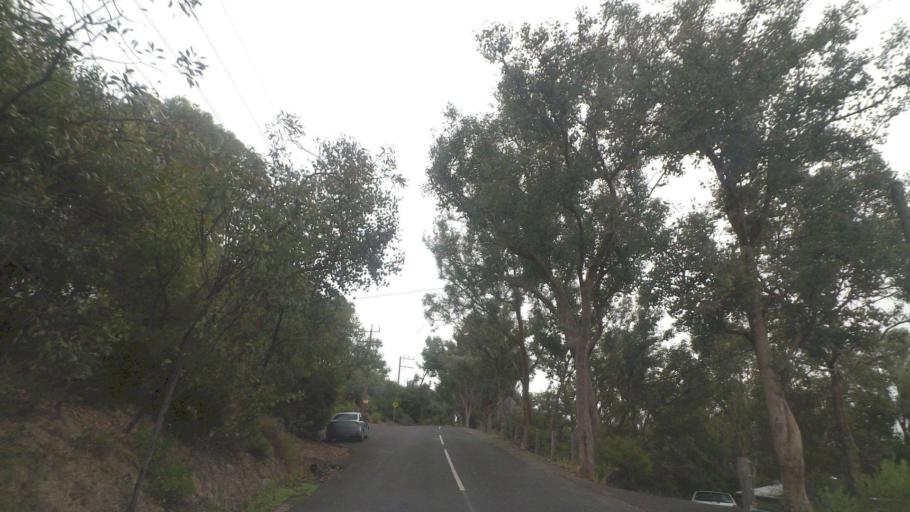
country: AU
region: Victoria
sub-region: Nillumbik
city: North Warrandyte
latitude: -37.7426
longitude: 145.2001
